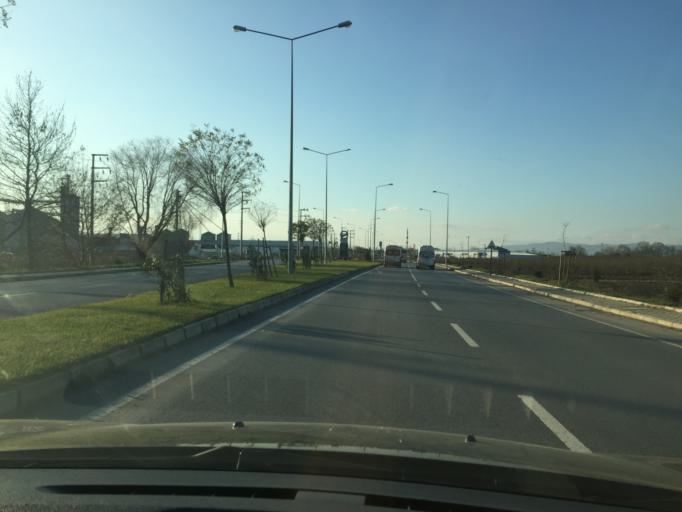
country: TR
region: Sakarya
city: Sogutlu
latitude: 40.9044
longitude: 30.4891
